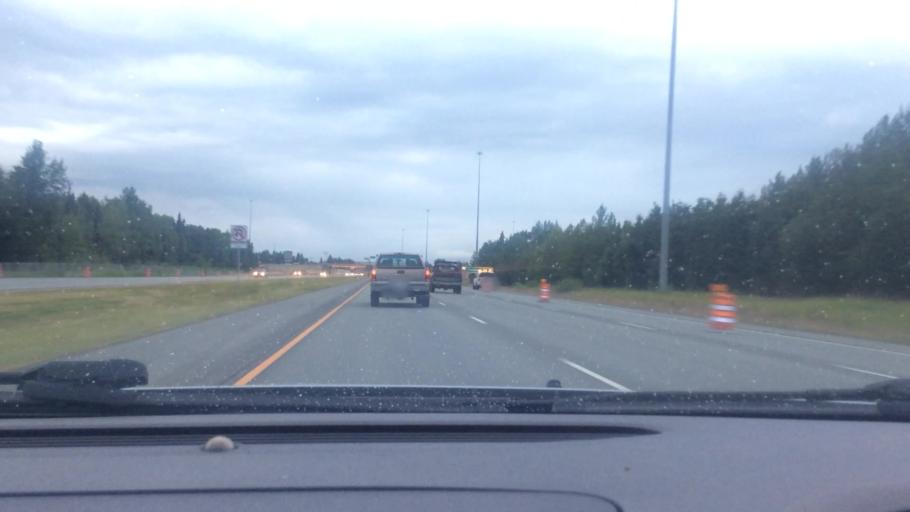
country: US
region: Alaska
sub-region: Anchorage Municipality
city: Elmendorf Air Force Base
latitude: 61.2299
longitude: -149.7208
